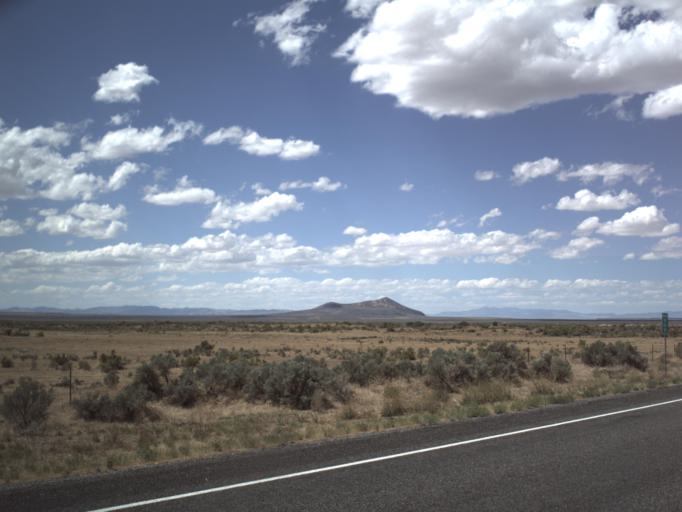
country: US
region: Utah
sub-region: Millard County
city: Fillmore
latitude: 39.1447
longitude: -112.3844
